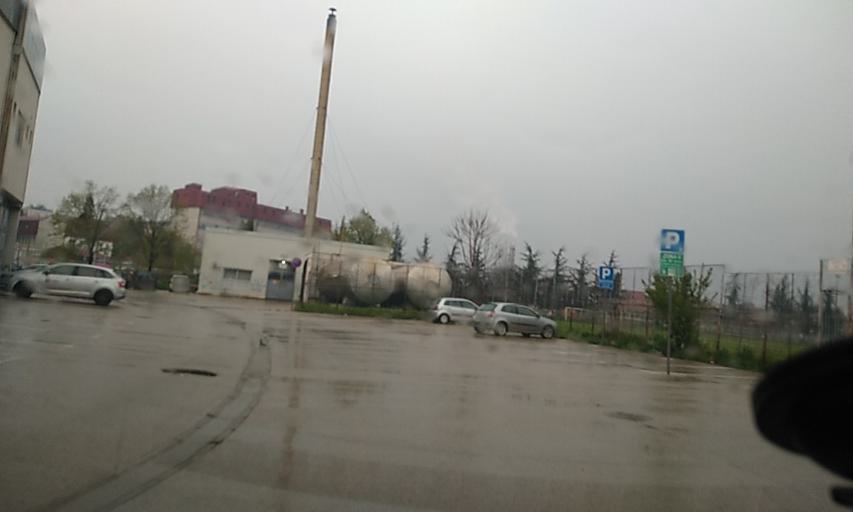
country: RS
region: Central Serbia
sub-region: Nisavski Okrug
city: Nis
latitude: 43.3145
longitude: 21.9090
